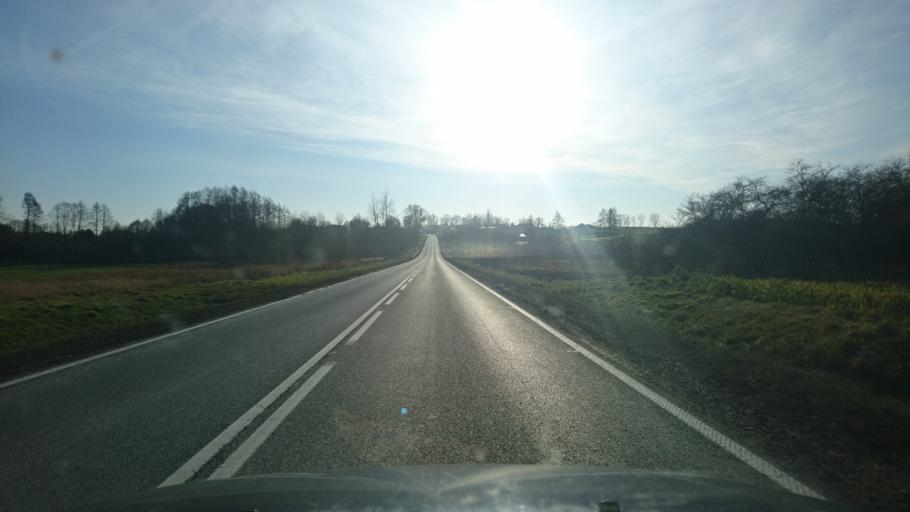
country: PL
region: Opole Voivodeship
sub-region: Powiat oleski
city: Dalachow
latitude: 51.0481
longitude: 18.5974
